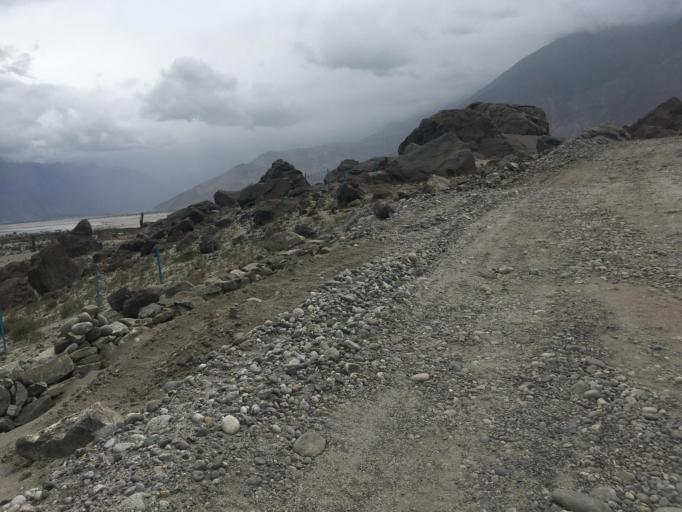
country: PK
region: Gilgit-Baltistan
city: Skardu
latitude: 35.3192
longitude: 75.6559
